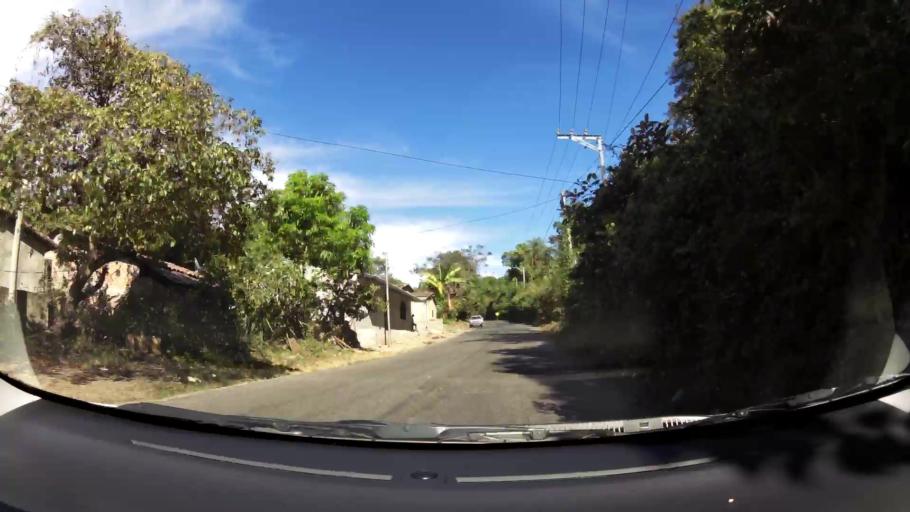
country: SV
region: Cuscatlan
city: Suchitoto
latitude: 13.9291
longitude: -89.0332
